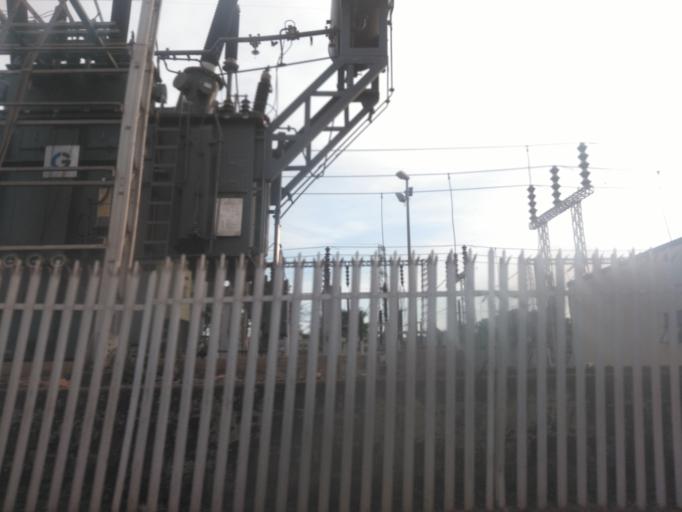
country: UG
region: Central Region
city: Kampala Central Division
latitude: 0.3475
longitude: 32.5753
